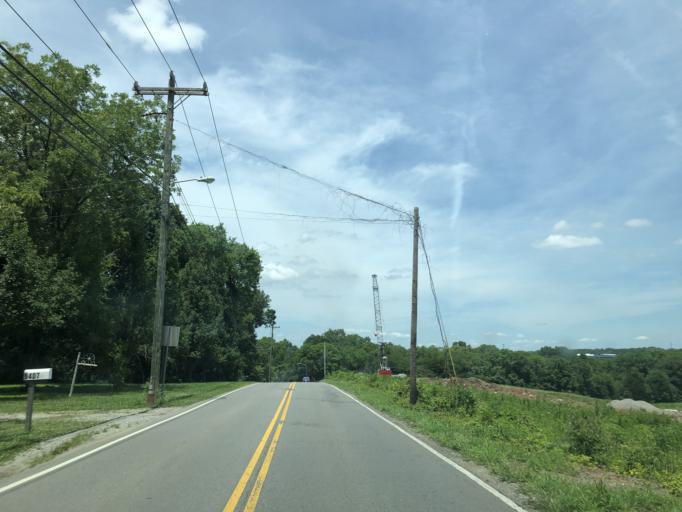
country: US
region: Tennessee
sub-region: Rutherford County
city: La Vergne
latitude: 36.0369
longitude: -86.6575
